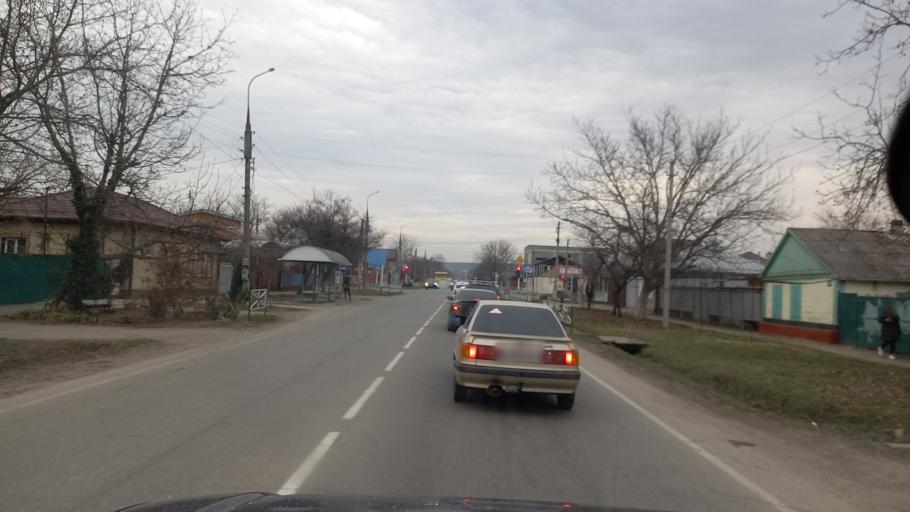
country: RU
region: Adygeya
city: Maykop
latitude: 44.5991
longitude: 40.1228
